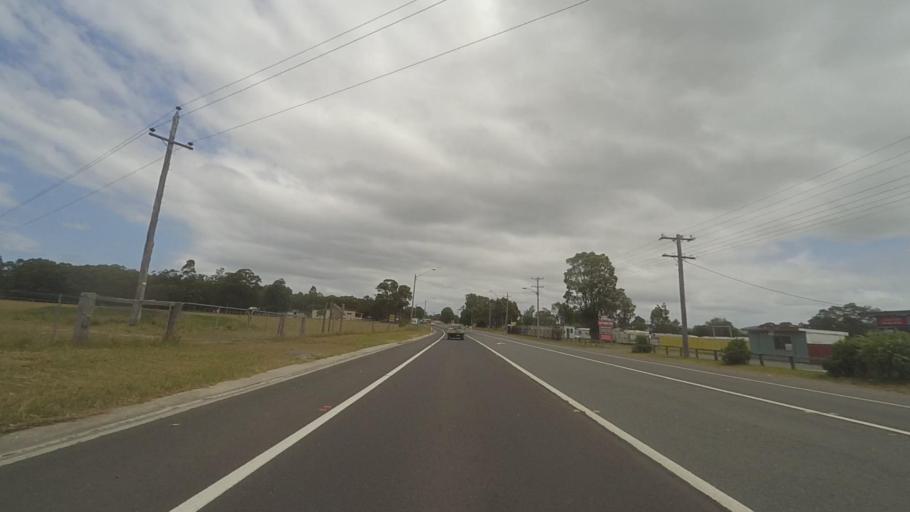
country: AU
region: New South Wales
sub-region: Shoalhaven Shire
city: Falls Creek
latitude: -35.0877
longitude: 150.5124
